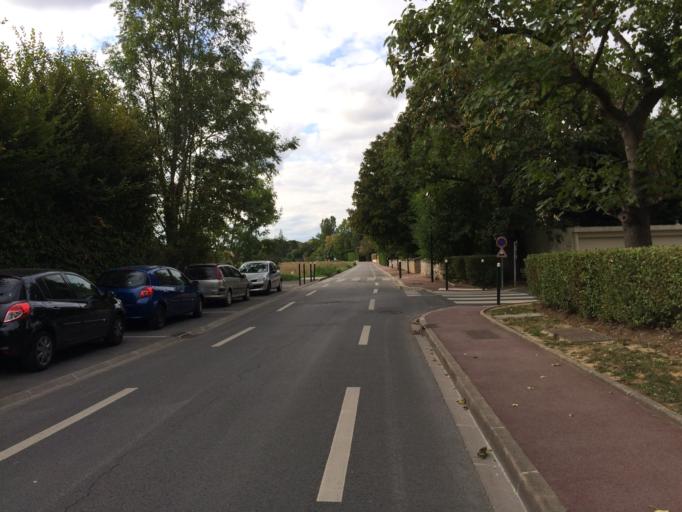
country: FR
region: Ile-de-France
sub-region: Departement de l'Essonne
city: Soisy-sur-Seine
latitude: 48.6500
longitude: 2.4413
